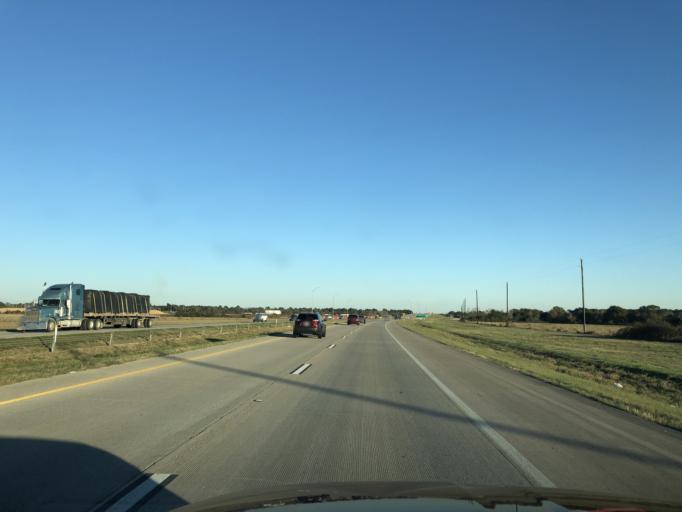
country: US
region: Texas
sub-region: Harris County
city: Cypress
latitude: 30.0544
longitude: -95.7083
